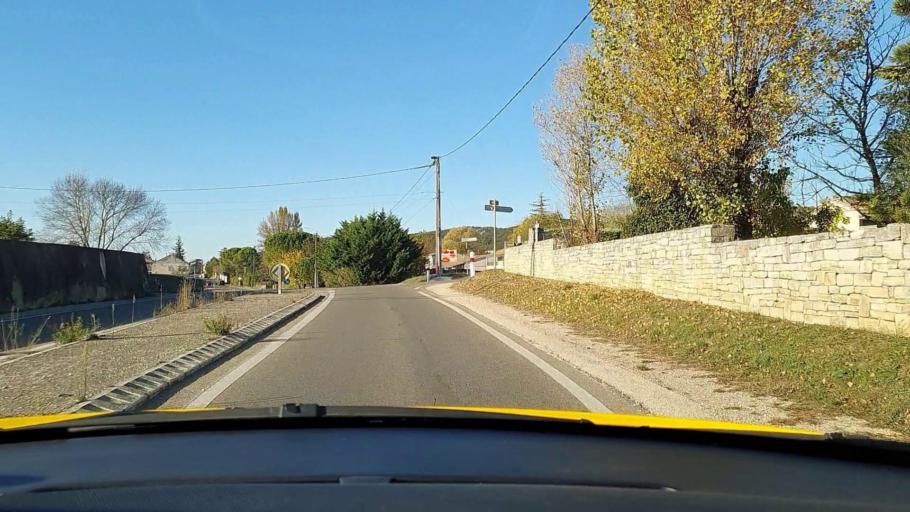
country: FR
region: Languedoc-Roussillon
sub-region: Departement du Gard
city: Saint-Privat-des-Vieux
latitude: 44.1683
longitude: 4.1338
